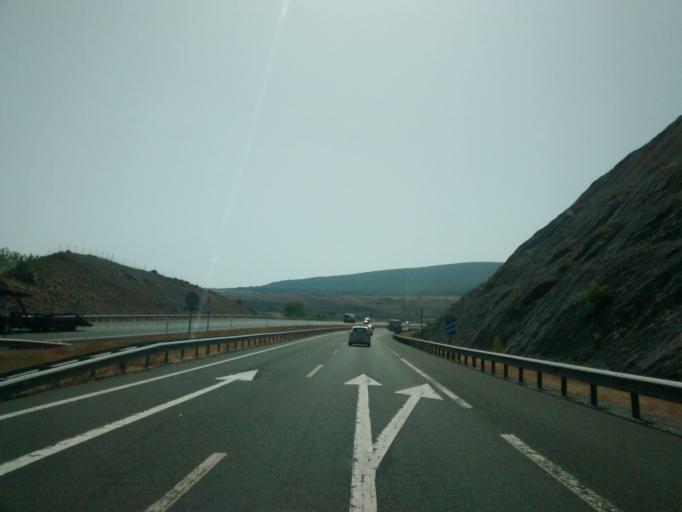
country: ES
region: Cantabria
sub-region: Provincia de Cantabria
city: Villaescusa
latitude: 42.9473
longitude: -4.1347
